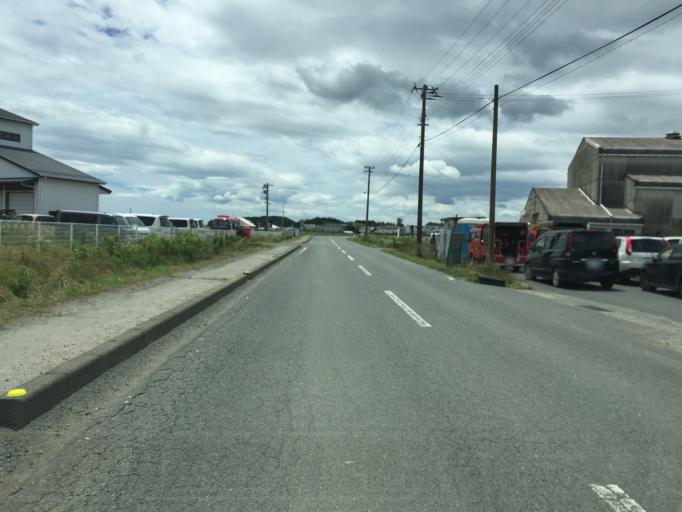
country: JP
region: Fukushima
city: Namie
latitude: 37.6240
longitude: 141.0004
